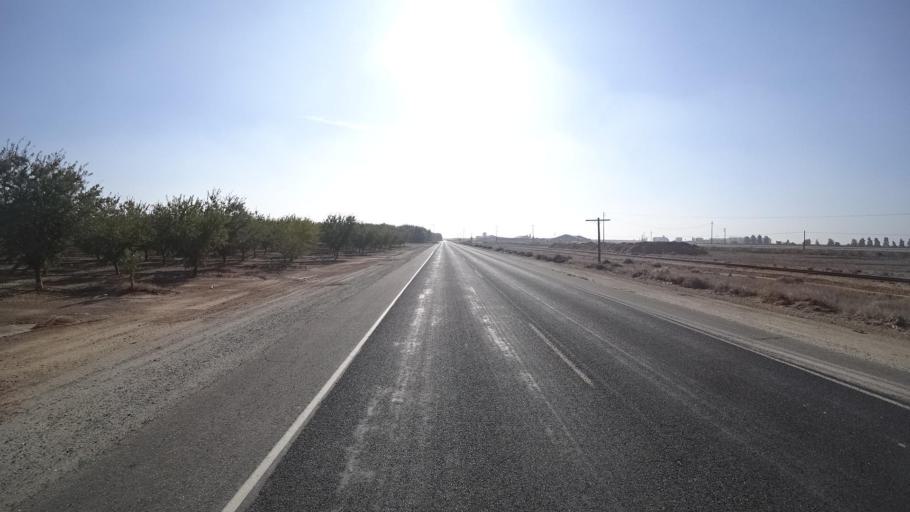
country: US
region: California
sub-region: Kern County
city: McFarland
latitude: 35.6399
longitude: -119.2031
